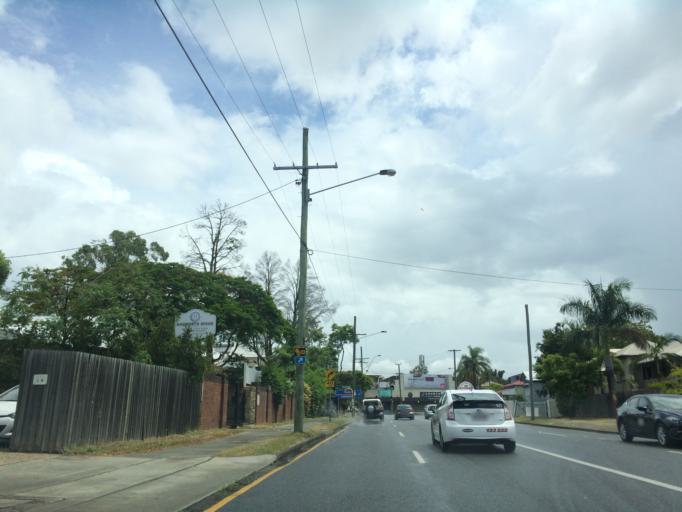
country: AU
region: Queensland
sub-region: Brisbane
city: Woolloongabba
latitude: -27.4787
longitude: 153.0476
